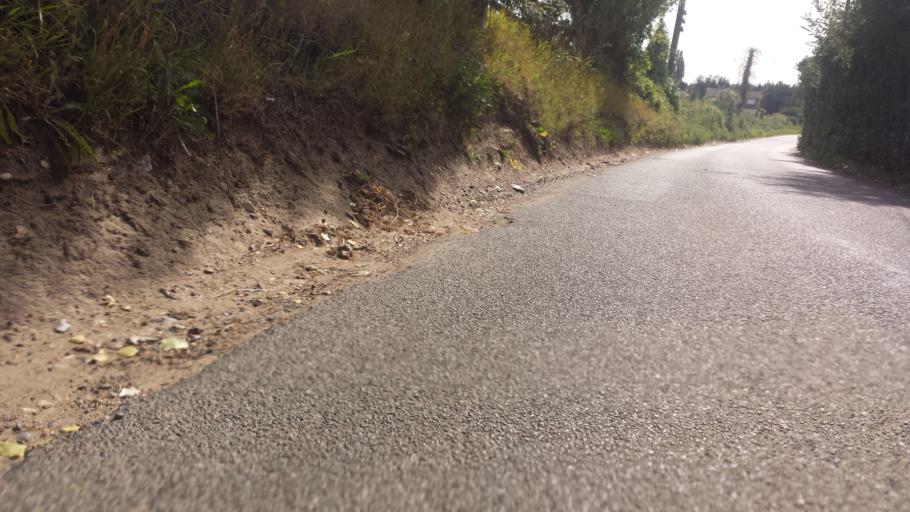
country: GB
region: England
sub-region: Kent
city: Swanley
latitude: 51.4015
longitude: 0.1487
